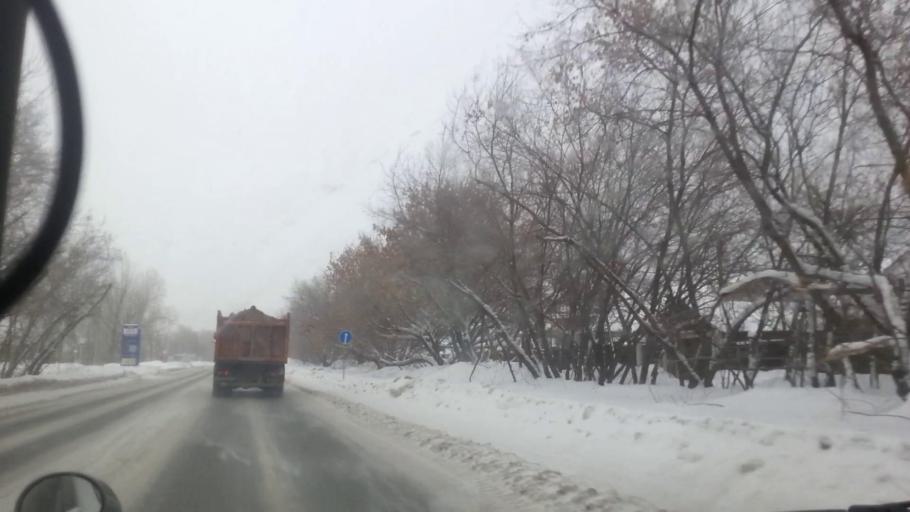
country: RU
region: Altai Krai
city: Vlasikha
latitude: 53.3011
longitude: 83.5982
